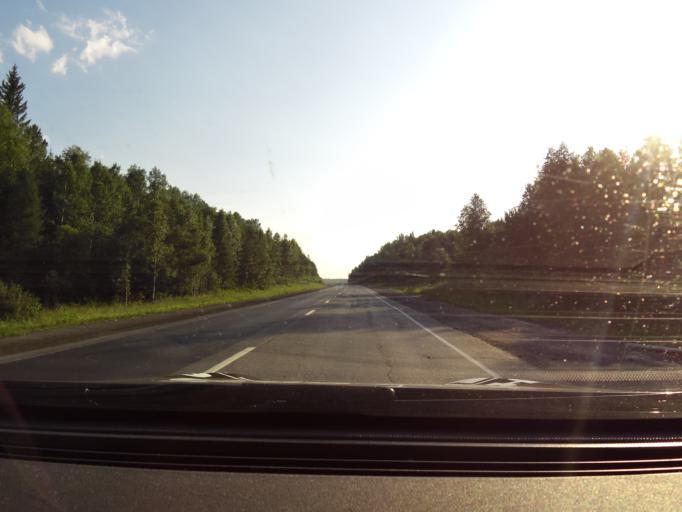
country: RU
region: Sverdlovsk
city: Druzhinino
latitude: 56.8365
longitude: 59.6450
